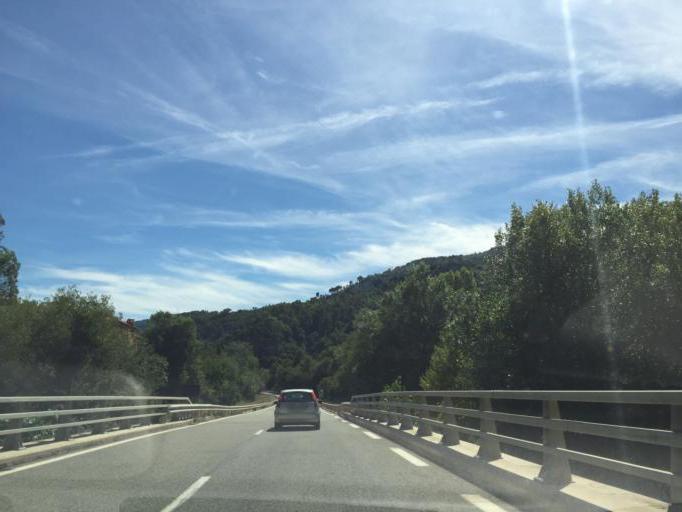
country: FR
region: Provence-Alpes-Cote d'Azur
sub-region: Departement des Alpes-Maritimes
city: Levens
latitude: 43.8596
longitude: 7.1975
